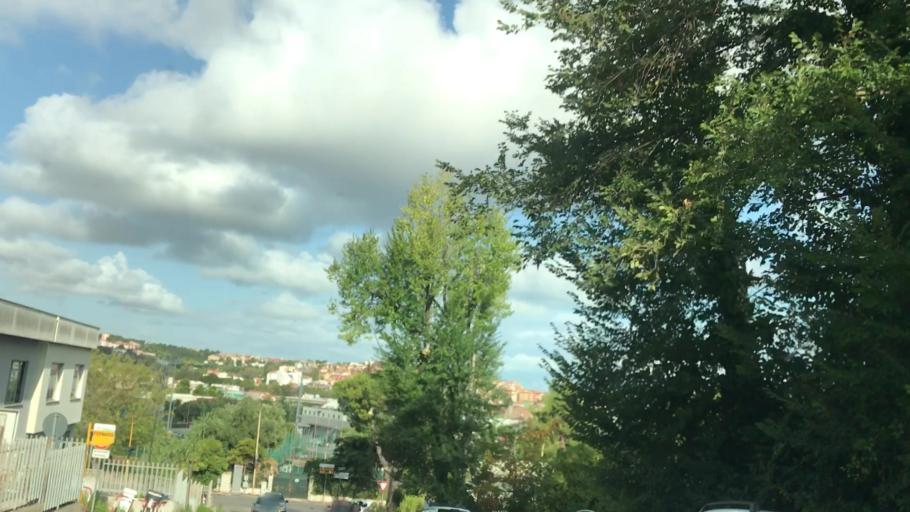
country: IT
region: The Marches
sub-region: Provincia di Ancona
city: Le Grazie di Ancona
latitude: 43.5951
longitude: 13.5137
